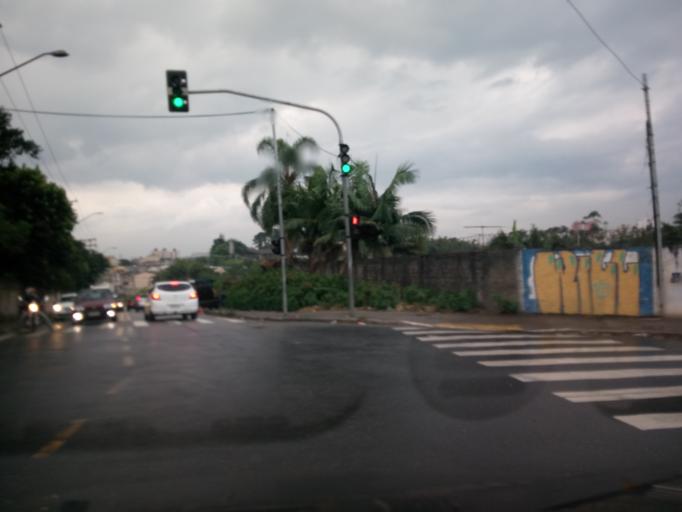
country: BR
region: Sao Paulo
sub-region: Sao Bernardo Do Campo
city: Sao Bernardo do Campo
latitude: -23.7251
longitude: -46.5883
